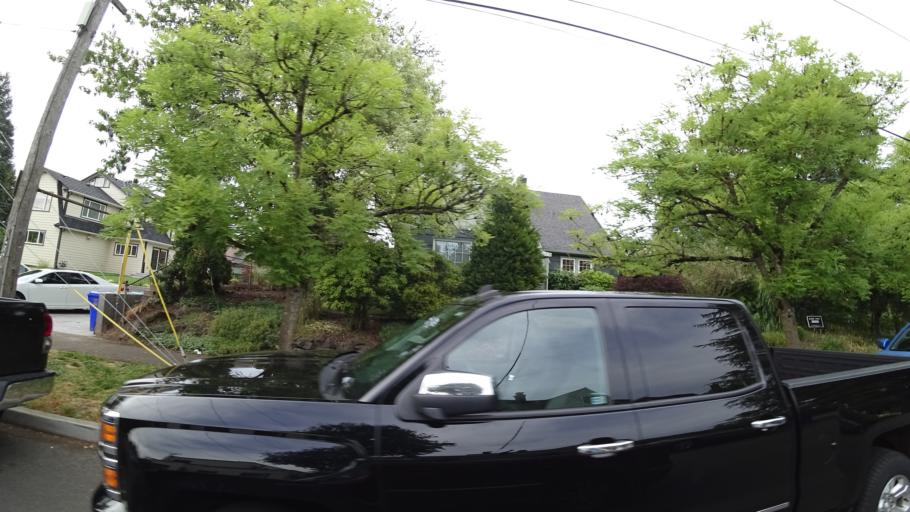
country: US
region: Oregon
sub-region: Multnomah County
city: Portland
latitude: 45.5613
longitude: -122.6945
